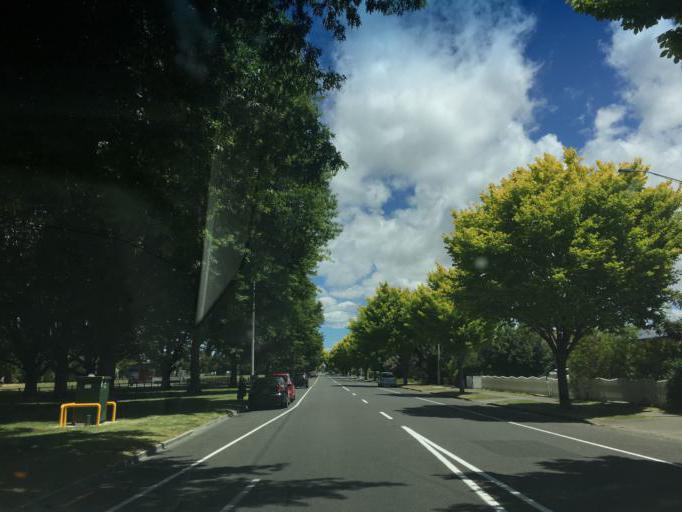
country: NZ
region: Hawke's Bay
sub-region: Hastings District
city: Hastings
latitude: -39.6423
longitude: 176.8629
